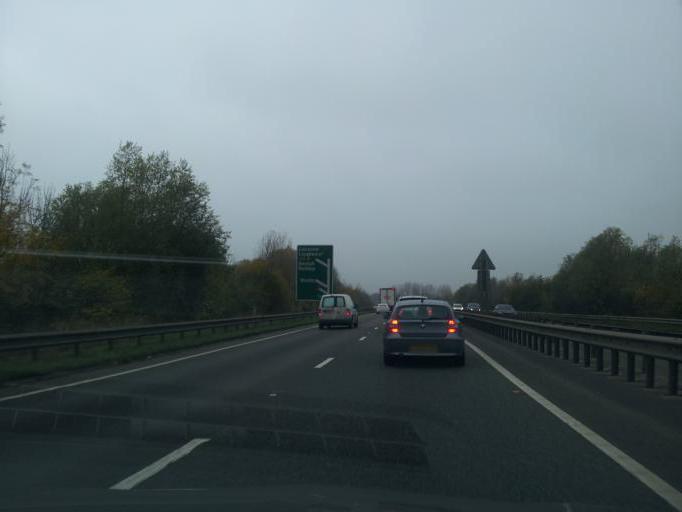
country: GB
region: England
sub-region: Leicestershire
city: Sileby
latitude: 52.6984
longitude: -1.1004
